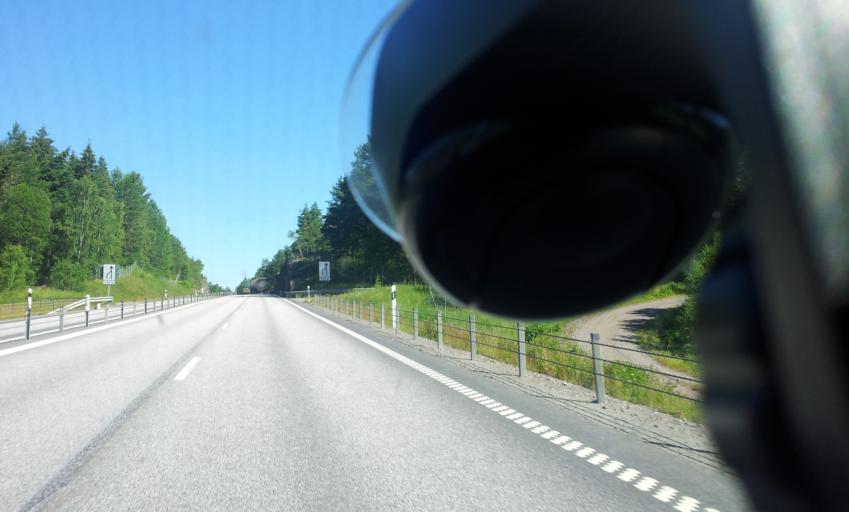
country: SE
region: OEstergoetland
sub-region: Valdemarsviks Kommun
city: Gusum
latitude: 58.3404
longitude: 16.4510
